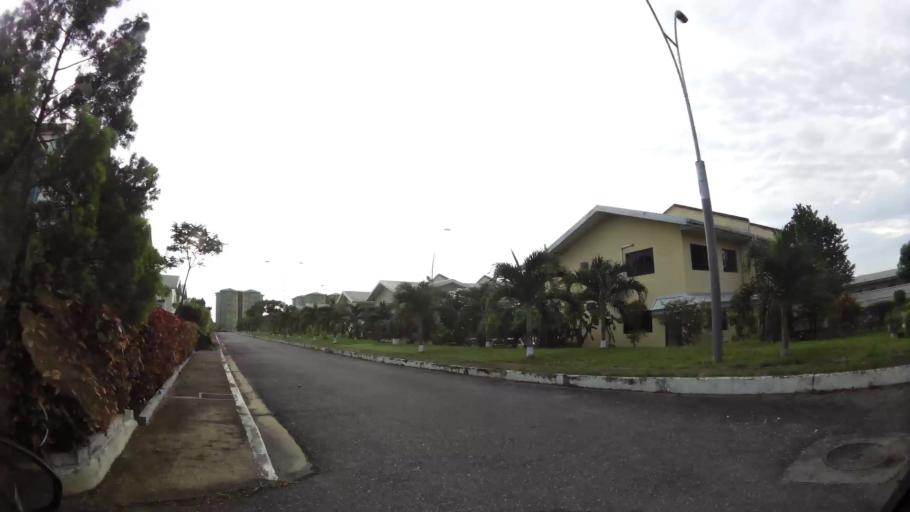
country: TT
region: Tunapuna/Piarco
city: Tunapuna
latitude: 10.6400
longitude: -61.4143
